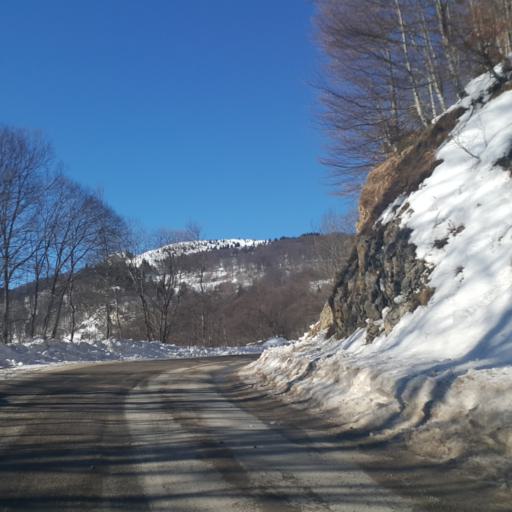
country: XK
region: Mitrovica
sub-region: Komuna e Leposaviqit
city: Leposaviq
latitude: 43.3147
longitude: 20.8583
